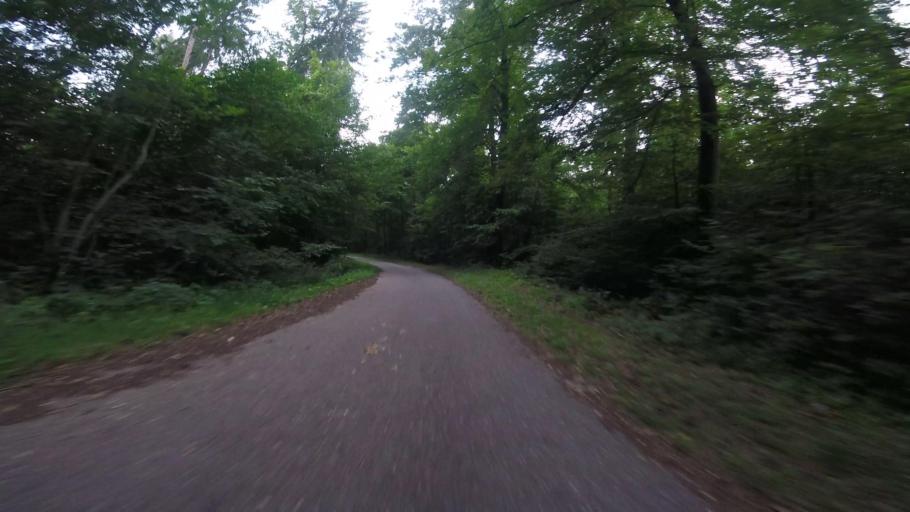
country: DE
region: Baden-Wuerttemberg
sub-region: Regierungsbezirk Stuttgart
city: Grossbottwar
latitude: 48.9901
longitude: 9.3183
